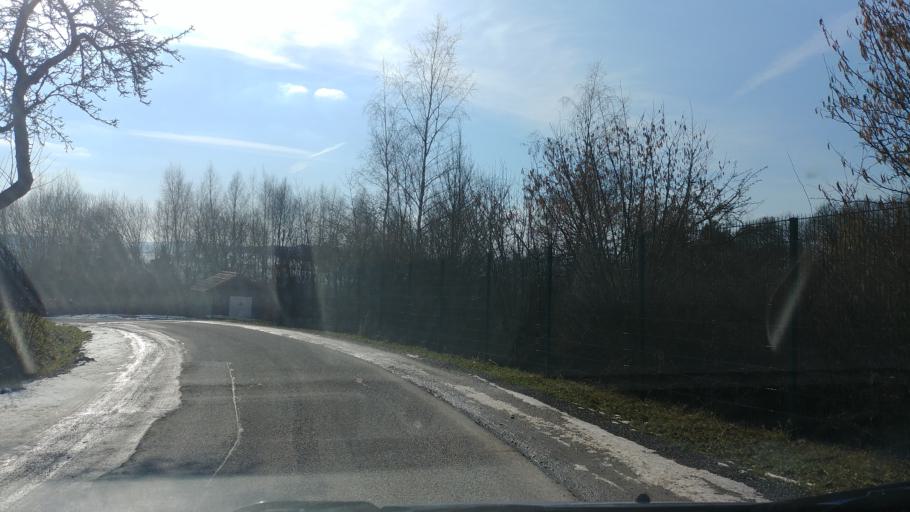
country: DE
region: Lower Saxony
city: Uslar
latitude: 51.6586
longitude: 9.6542
